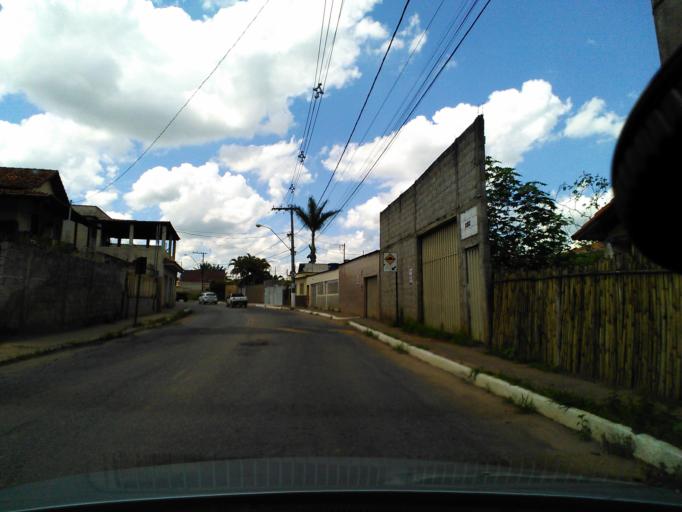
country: BR
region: Minas Gerais
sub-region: Tres Coracoes
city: Tres Coracoes
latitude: -21.7171
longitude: -45.2626
